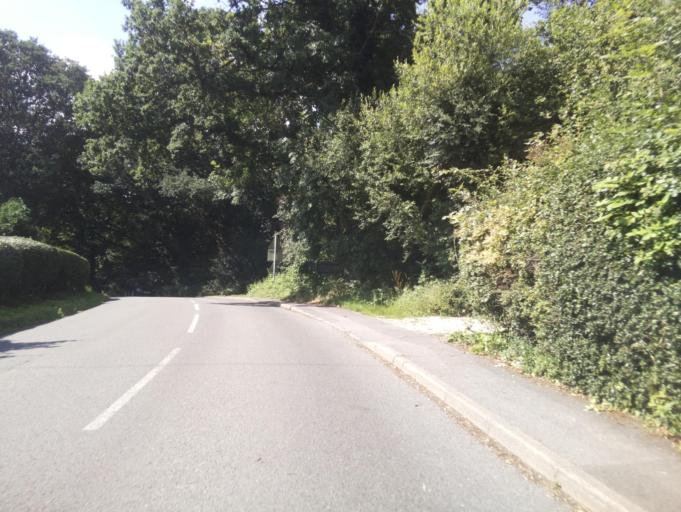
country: GB
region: England
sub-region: West Berkshire
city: Greenham
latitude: 51.3693
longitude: -1.2828
